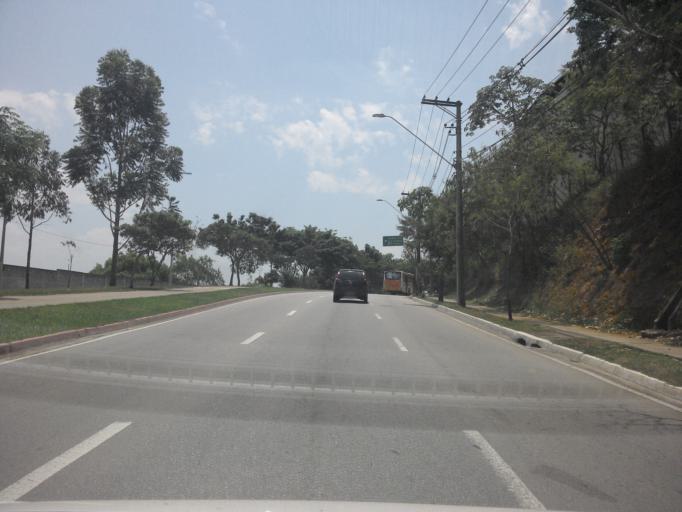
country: BR
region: Sao Paulo
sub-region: Sao Jose Dos Campos
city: Sao Jose dos Campos
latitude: -23.1665
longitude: -45.8076
